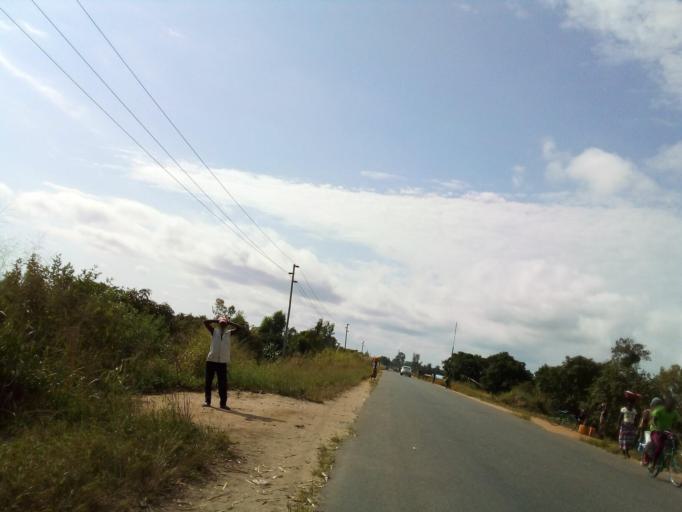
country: MZ
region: Zambezia
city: Quelimane
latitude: -17.5780
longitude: 36.6936
